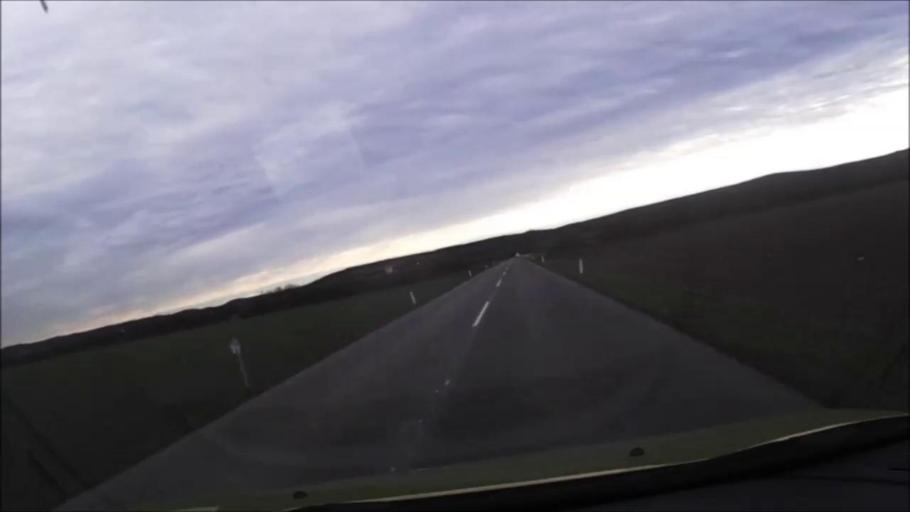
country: AT
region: Burgenland
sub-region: Eisenstadt-Umgebung
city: Leithaprodersdorf
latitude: 47.9270
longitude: 16.4991
